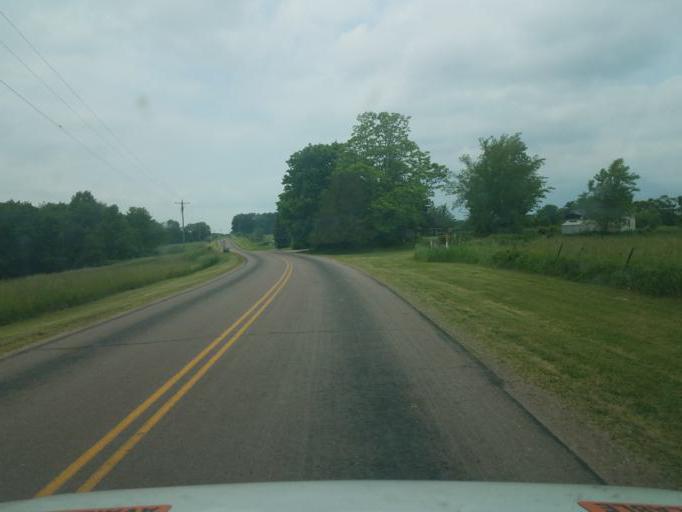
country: US
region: Wisconsin
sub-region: Vernon County
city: Hillsboro
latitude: 43.5916
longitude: -90.3864
